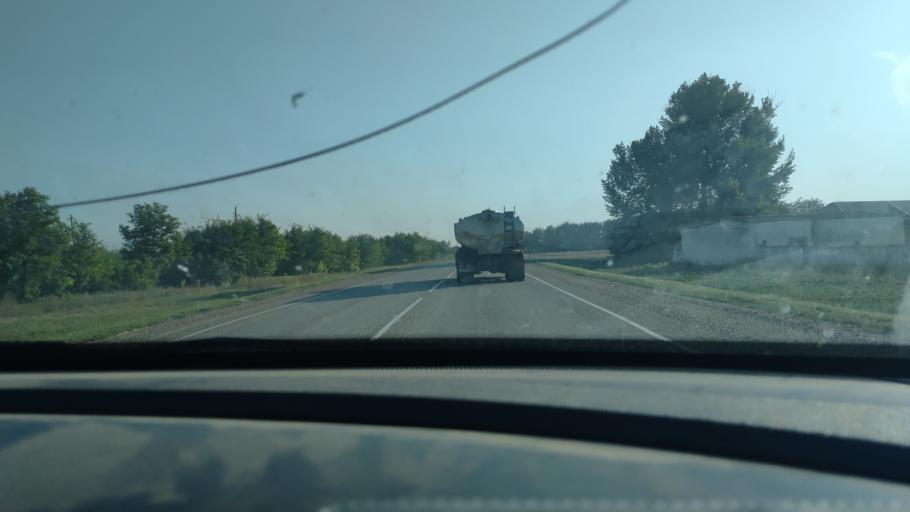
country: RU
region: Krasnodarskiy
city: Starominskaya
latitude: 46.4493
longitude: 39.0289
